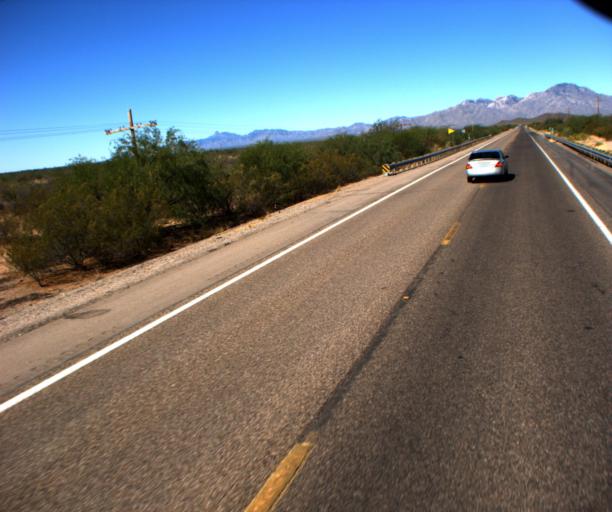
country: US
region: Arizona
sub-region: Pima County
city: Three Points
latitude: 32.0728
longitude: -111.3524
